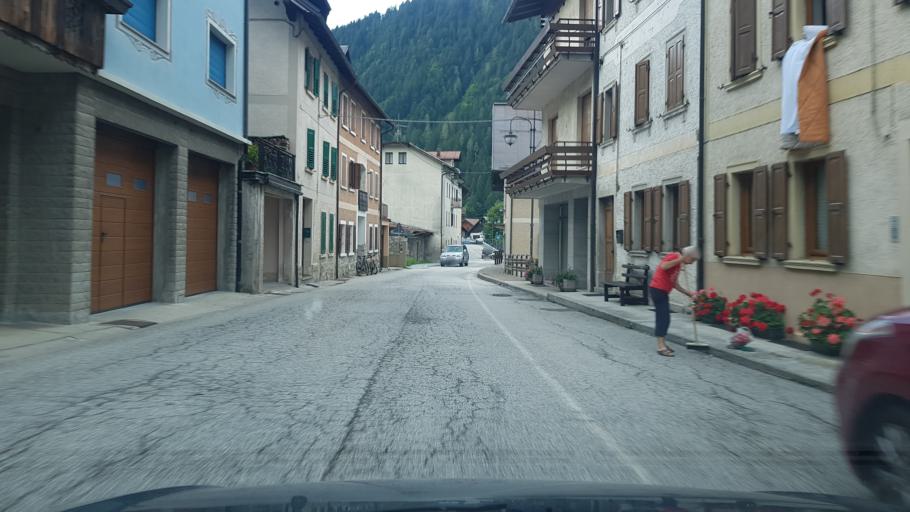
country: IT
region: Friuli Venezia Giulia
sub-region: Provincia di Udine
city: Forni Avoltri
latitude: 46.5867
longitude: 12.7762
